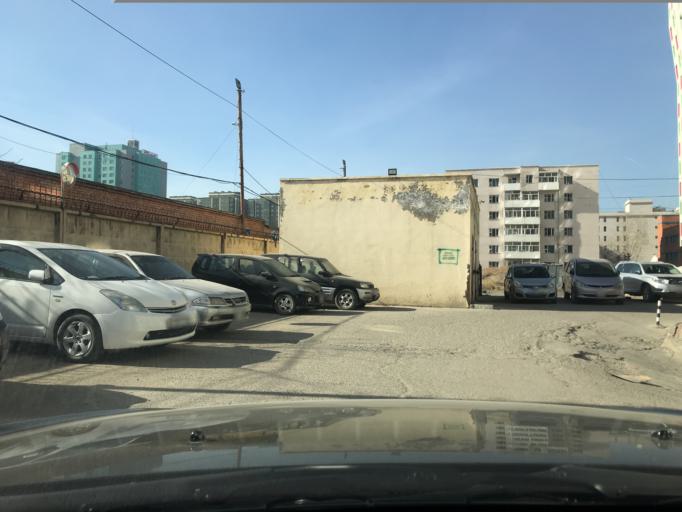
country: MN
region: Ulaanbaatar
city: Ulaanbaatar
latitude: 47.9112
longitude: 106.9471
